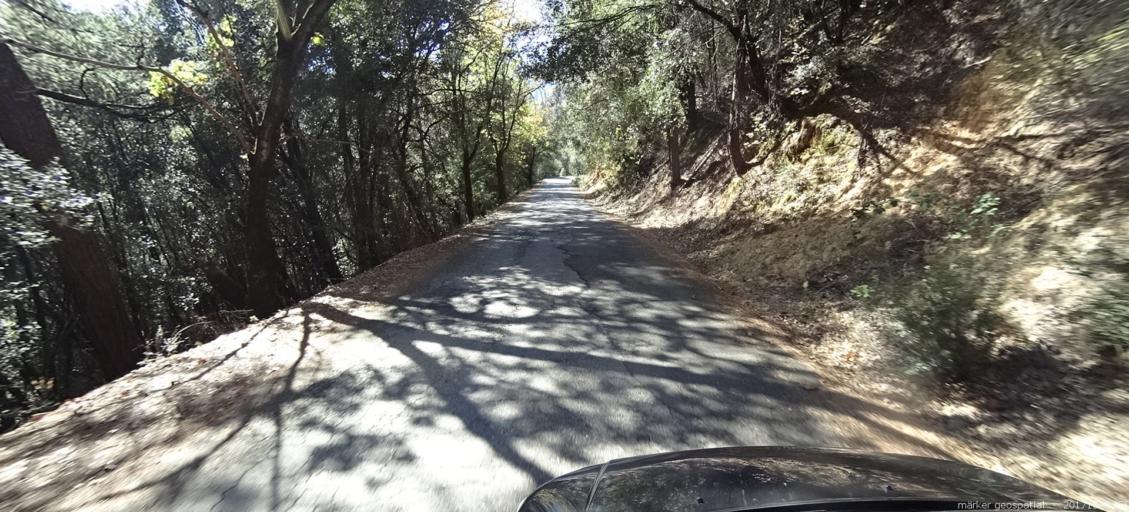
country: US
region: California
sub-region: Trinity County
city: Lewiston
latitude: 40.7941
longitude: -122.6117
